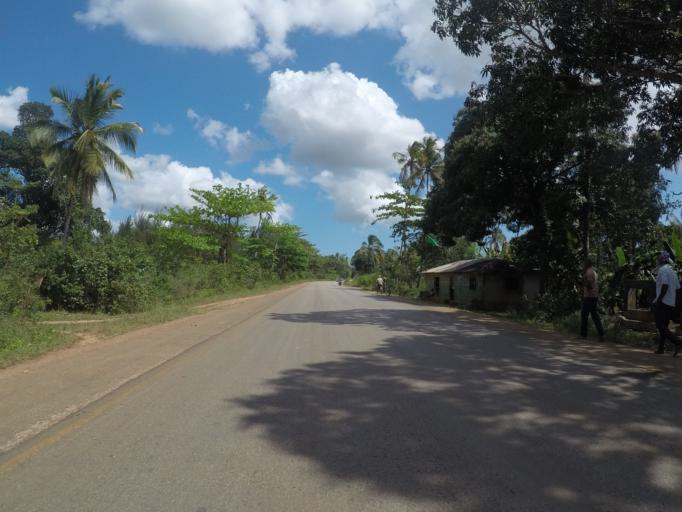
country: TZ
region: Zanzibar Central/South
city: Koani
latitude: -6.1690
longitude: 39.3302
